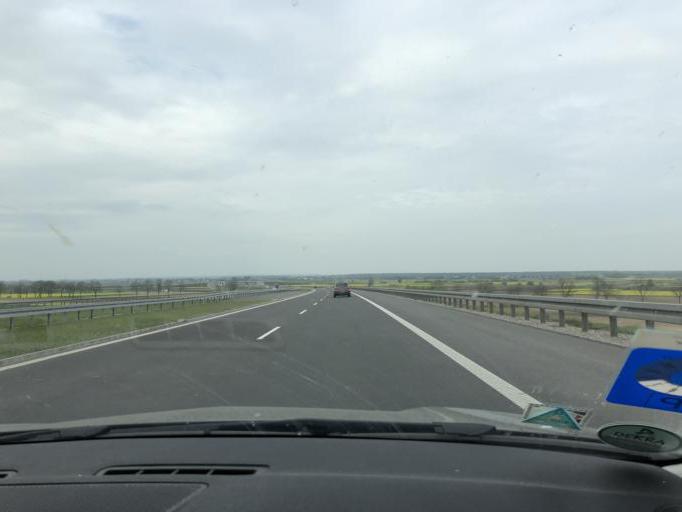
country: PL
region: Subcarpathian Voivodeship
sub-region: Powiat przeworski
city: Rozborz
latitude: 50.0653
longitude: 22.5628
